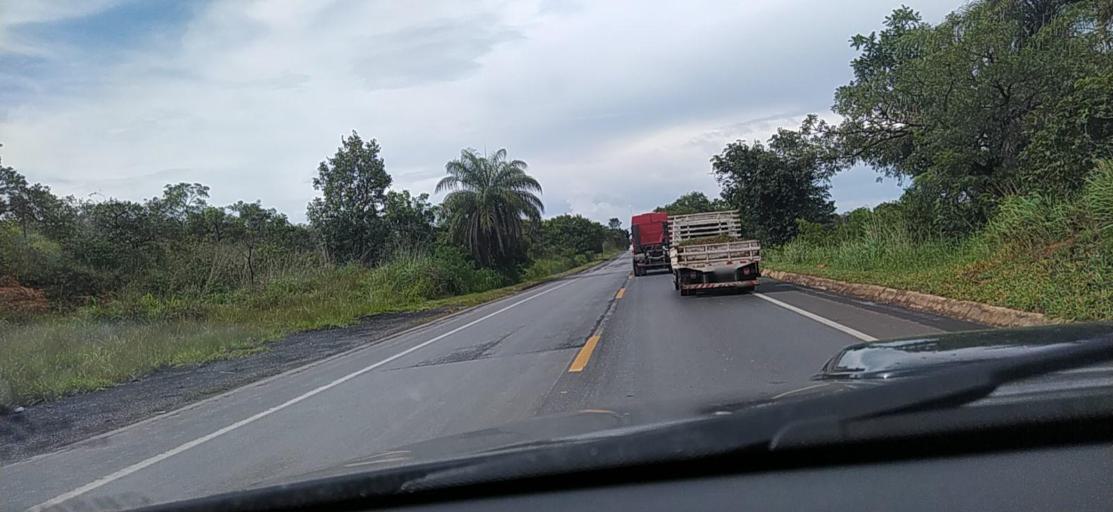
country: BR
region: Minas Gerais
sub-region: Montes Claros
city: Montes Claros
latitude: -16.8526
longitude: -43.8524
